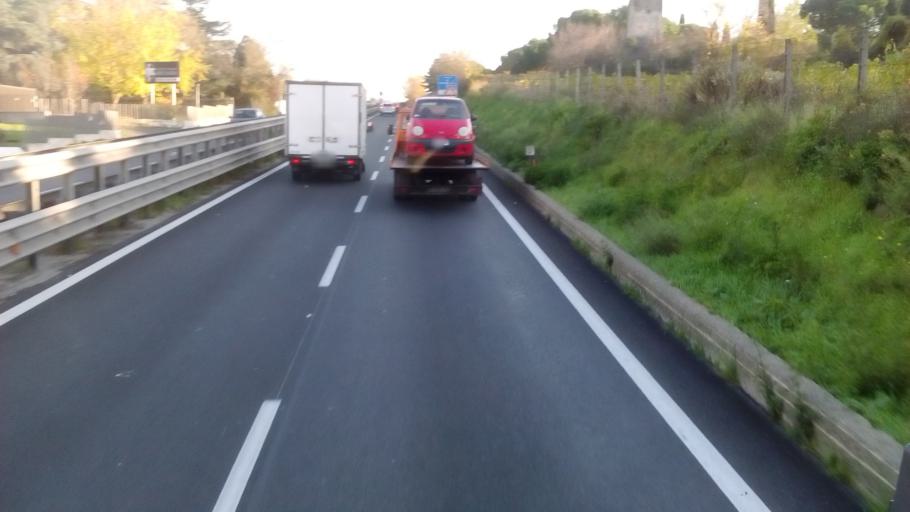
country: IT
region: Latium
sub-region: Citta metropolitana di Roma Capitale
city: Marino
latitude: 41.7701
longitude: 12.6133
